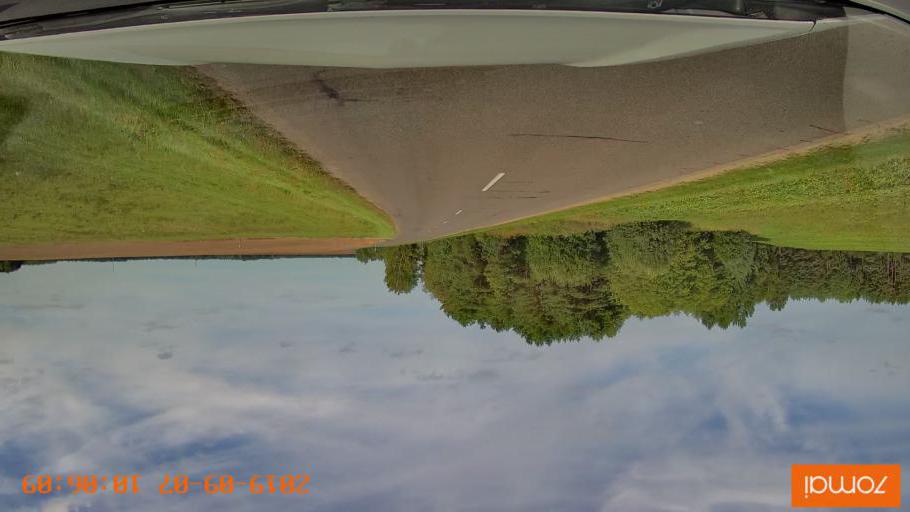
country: BY
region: Grodnenskaya
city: Voranava
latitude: 54.0572
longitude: 25.4037
